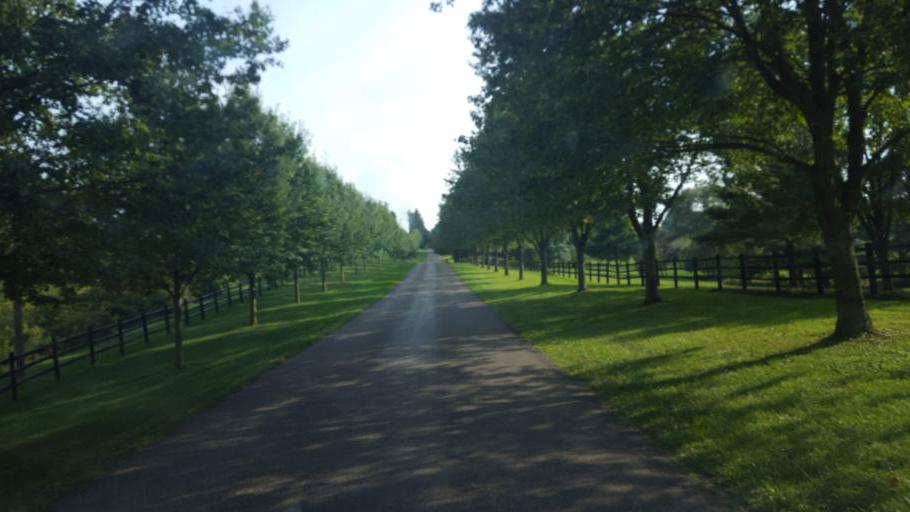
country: US
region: Ohio
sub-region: Knox County
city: Gambier
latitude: 40.3588
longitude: -82.4098
